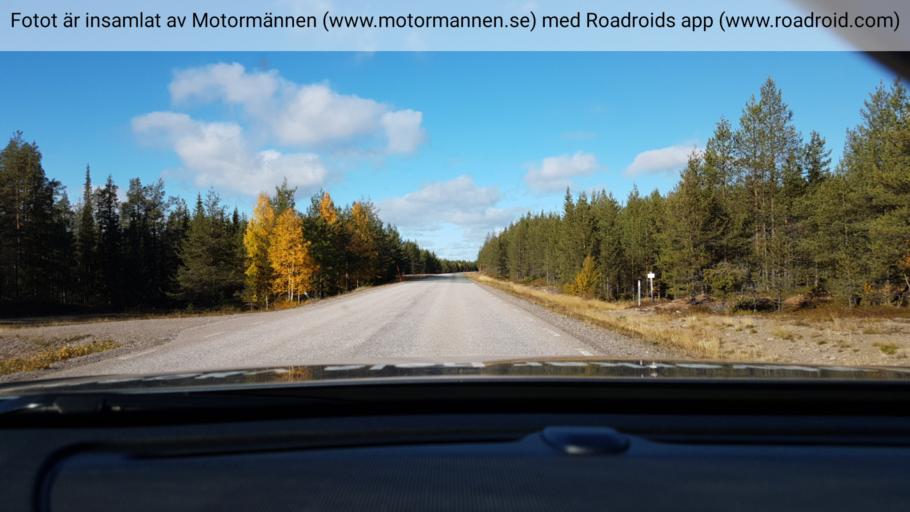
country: SE
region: Norrbotten
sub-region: Arvidsjaurs Kommun
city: Arvidsjaur
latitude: 65.7296
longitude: 18.6564
